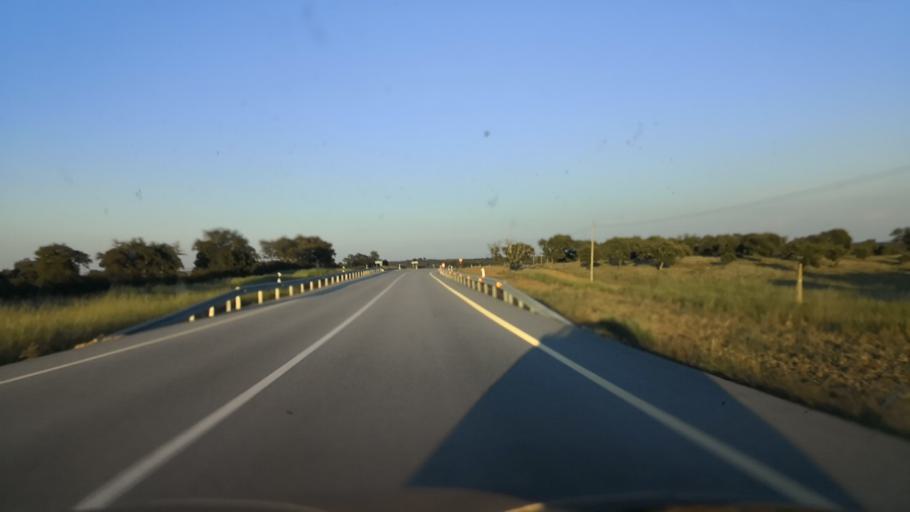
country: ES
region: Extremadura
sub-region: Provincia de Caceres
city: Salorino
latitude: 39.5107
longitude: -7.1045
